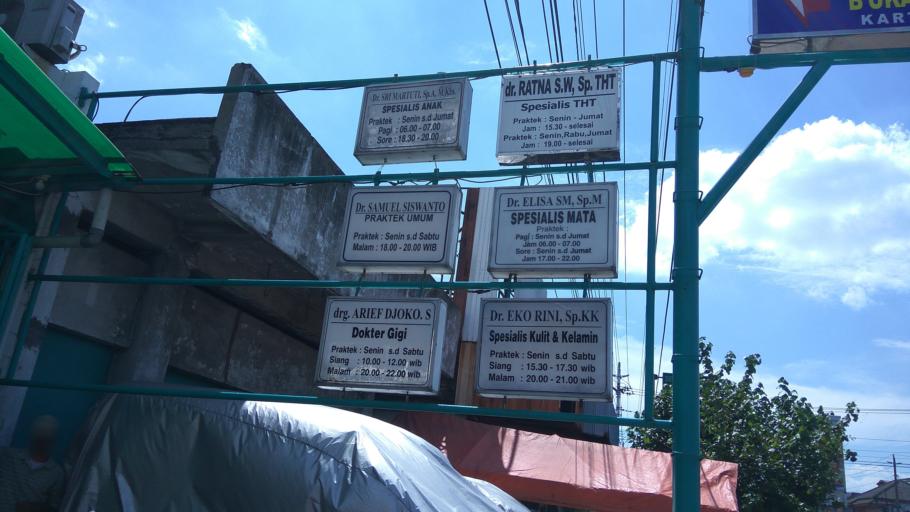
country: ID
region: Central Java
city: Kartasura
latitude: -7.5530
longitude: 110.7434
